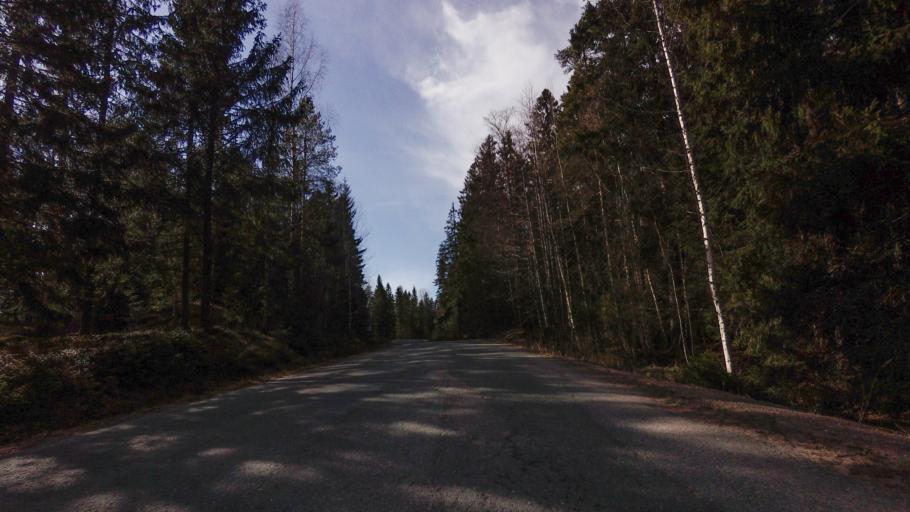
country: FI
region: Varsinais-Suomi
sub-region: Salo
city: Suomusjaervi
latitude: 60.3506
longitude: 23.6651
